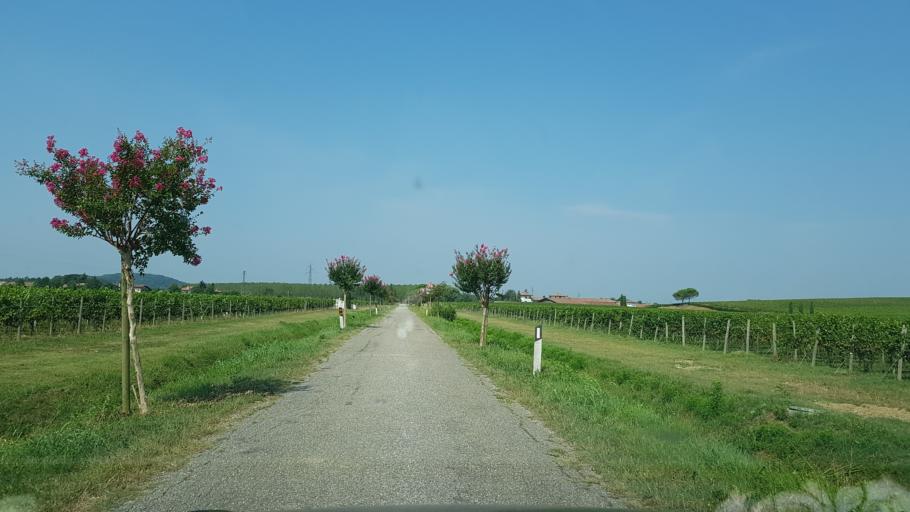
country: IT
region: Friuli Venezia Giulia
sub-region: Provincia di Gorizia
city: Moraro
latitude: 45.9341
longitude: 13.4857
